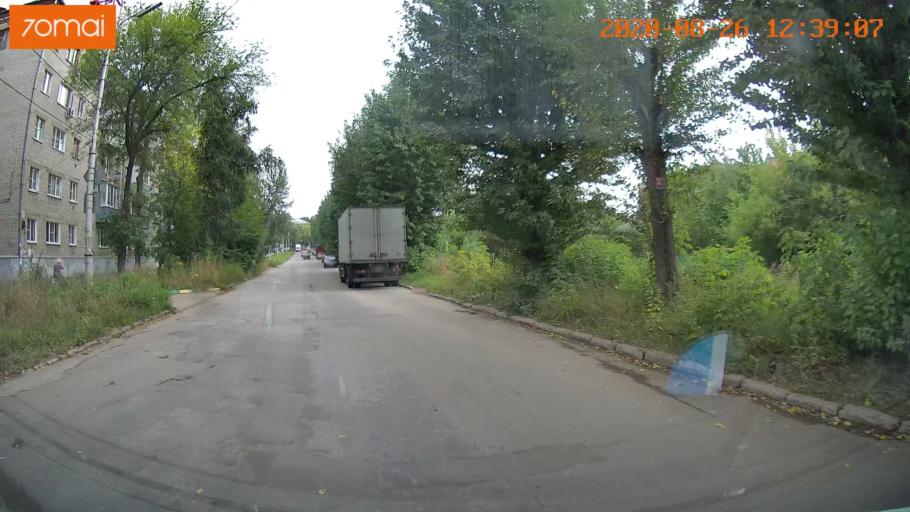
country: RU
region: Rjazan
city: Ryazan'
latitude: 54.6075
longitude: 39.7576
